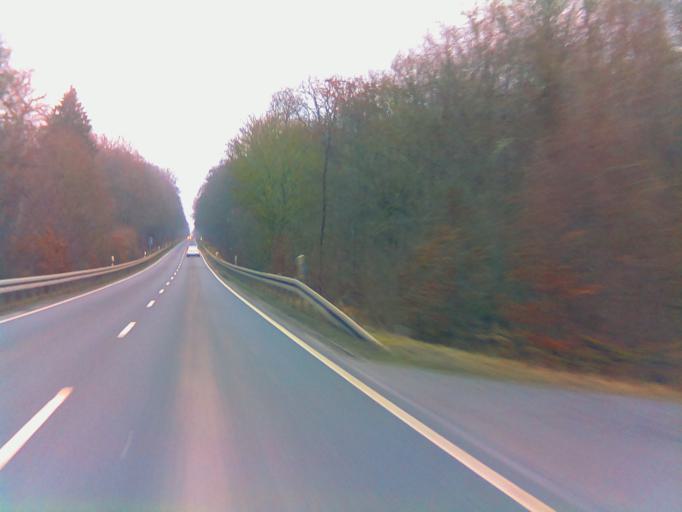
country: DE
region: Bavaria
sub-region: Regierungsbezirk Unterfranken
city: Rimpar
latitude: 49.9107
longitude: 9.9719
